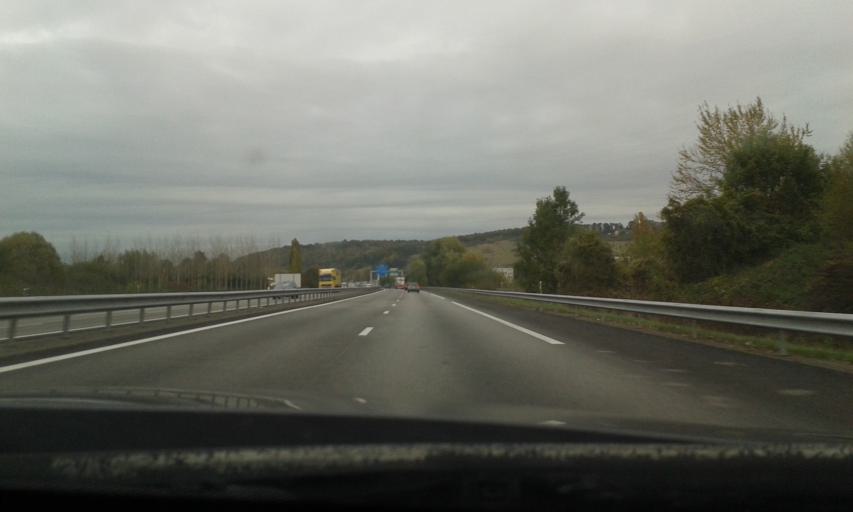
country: FR
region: Haute-Normandie
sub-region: Departement de l'Eure
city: Louviers
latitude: 49.2018
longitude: 1.1776
